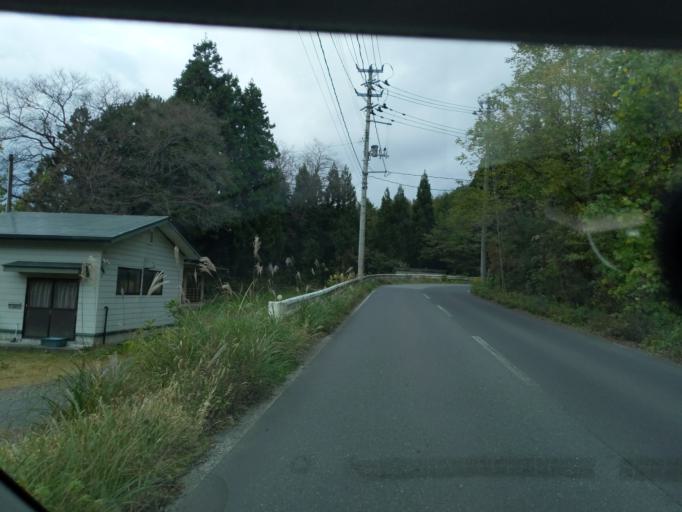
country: JP
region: Iwate
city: Mizusawa
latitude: 39.0495
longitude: 141.1128
